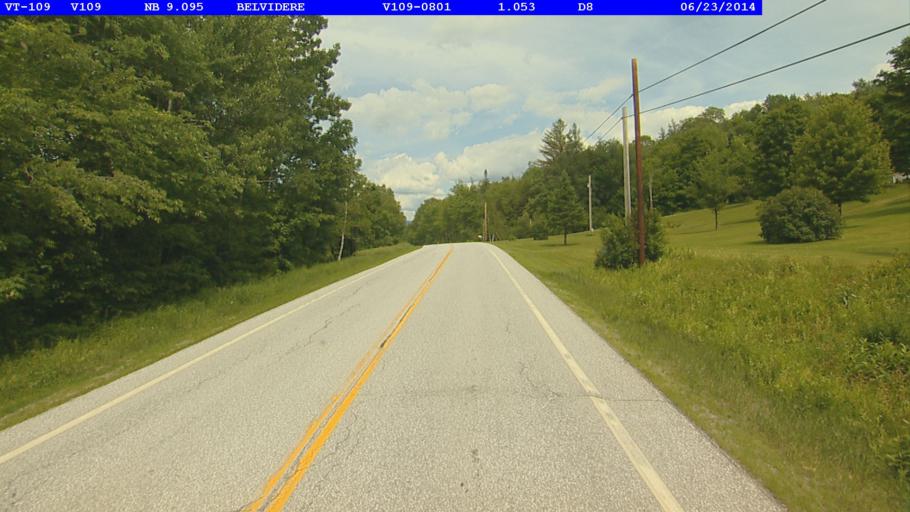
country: US
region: Vermont
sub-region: Lamoille County
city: Johnson
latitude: 44.7426
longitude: -72.7253
